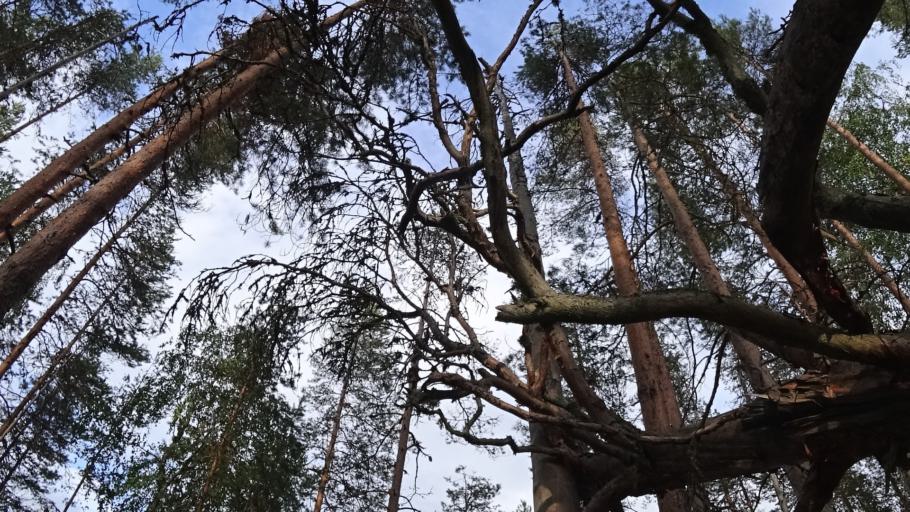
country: FI
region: North Karelia
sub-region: Joensuu
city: Ilomantsi
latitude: 62.5683
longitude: 31.1807
